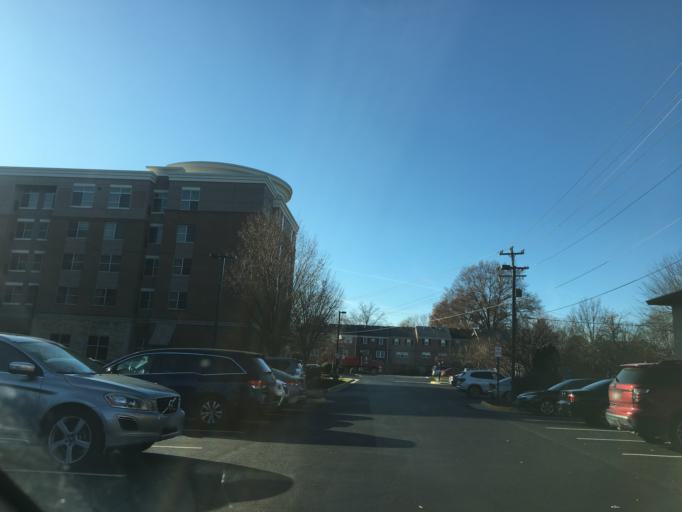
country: US
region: Virginia
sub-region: City of Fairfax
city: Fairfax
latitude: 38.8606
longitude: -77.3061
